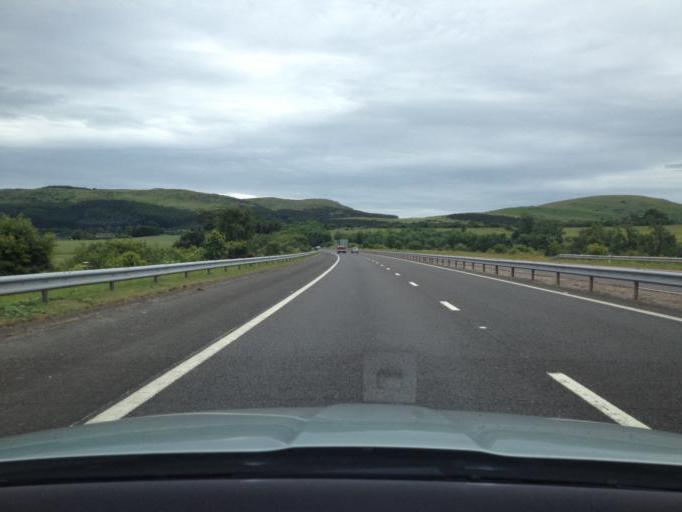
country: GB
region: Scotland
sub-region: Perth and Kinross
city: Bridge of Earn
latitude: 56.3335
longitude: -3.3998
